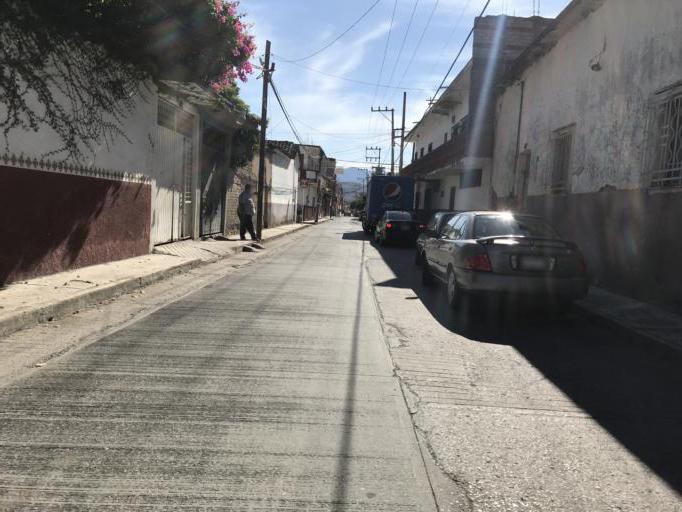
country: MX
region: Guerrero
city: Iguala de la Independencia
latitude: 18.3486
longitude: -99.5442
